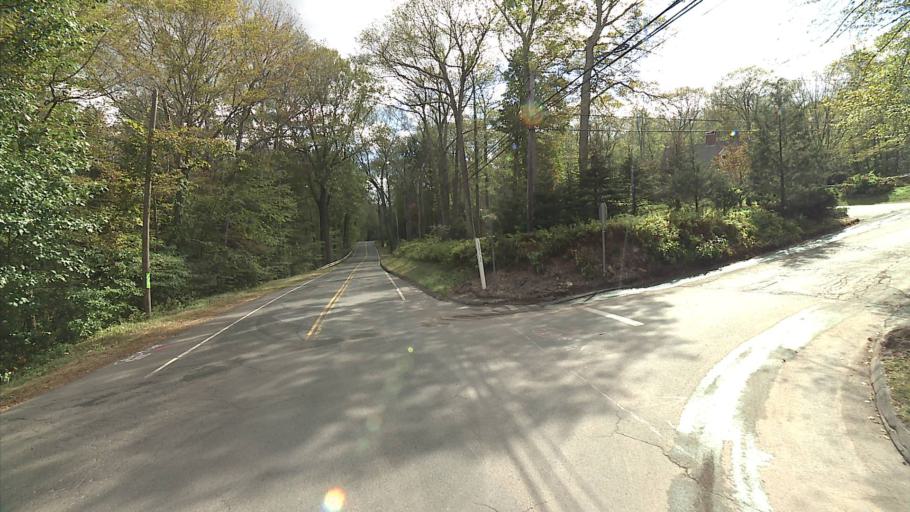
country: US
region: Connecticut
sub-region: Middlesex County
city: Durham
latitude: 41.4173
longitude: -72.6190
